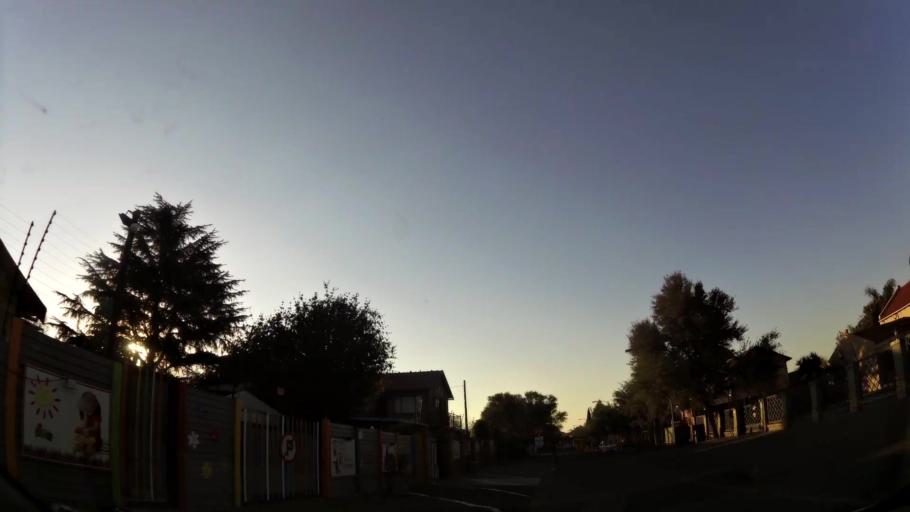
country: ZA
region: Gauteng
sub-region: City of Tshwane Metropolitan Municipality
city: Centurion
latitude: -25.8721
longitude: 28.1567
